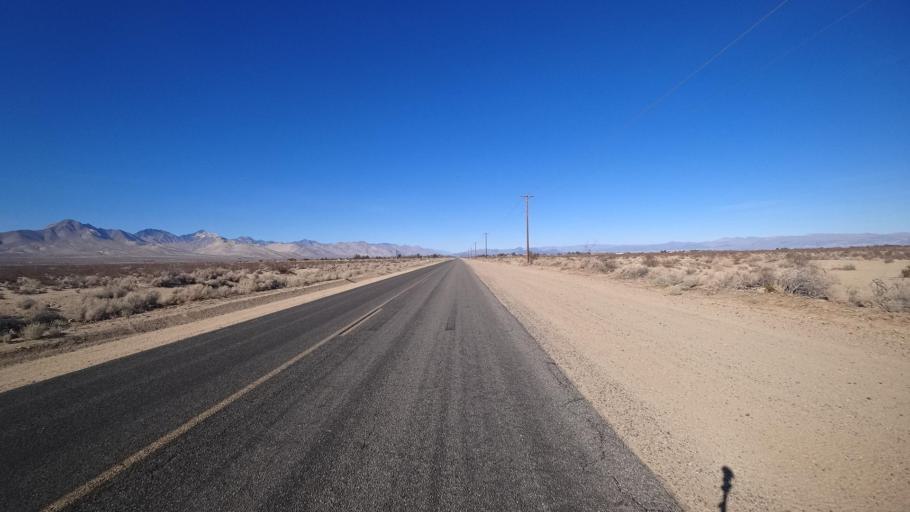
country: US
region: California
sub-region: Kern County
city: Inyokern
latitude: 35.6121
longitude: -117.8020
